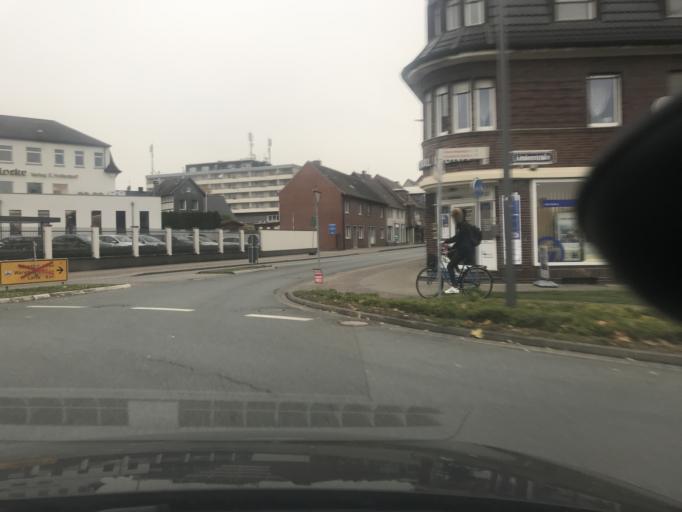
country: DE
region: North Rhine-Westphalia
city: Oelde
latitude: 51.8276
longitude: 8.1462
